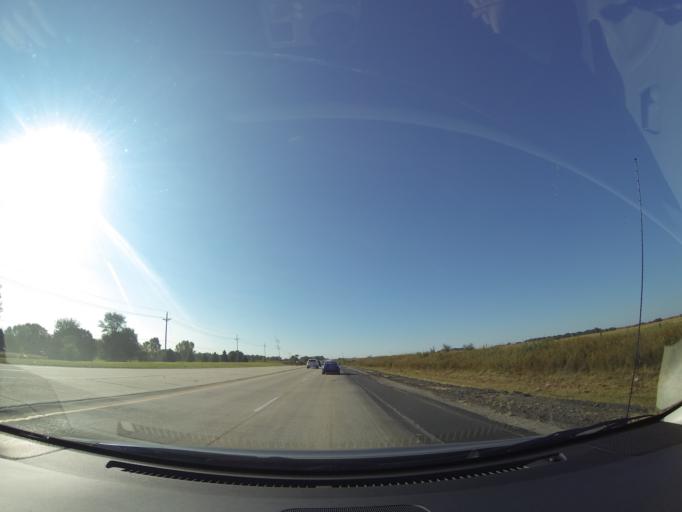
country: US
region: Nebraska
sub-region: Douglas County
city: Elkhorn
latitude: 41.2182
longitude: -96.2345
